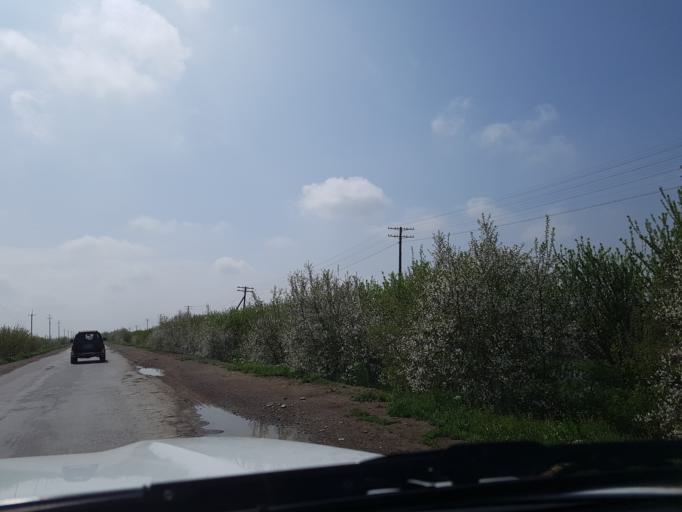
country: TM
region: Lebap
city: Turkmenabat
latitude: 38.9631
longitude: 63.6787
